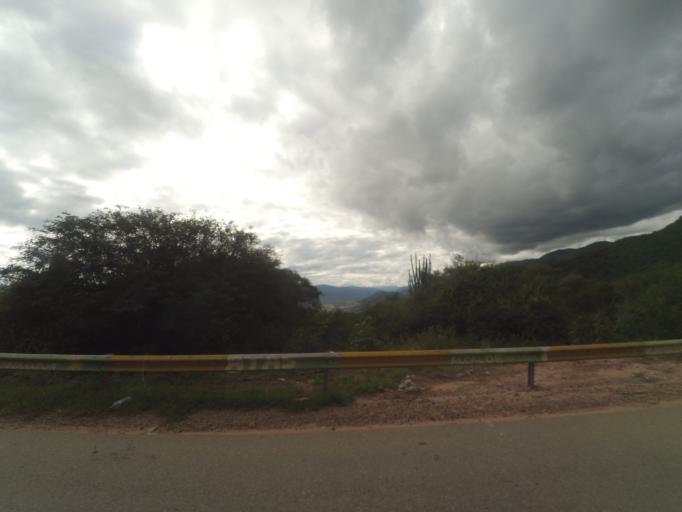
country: BO
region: Santa Cruz
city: Samaipata
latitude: -18.1668
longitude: -63.8924
